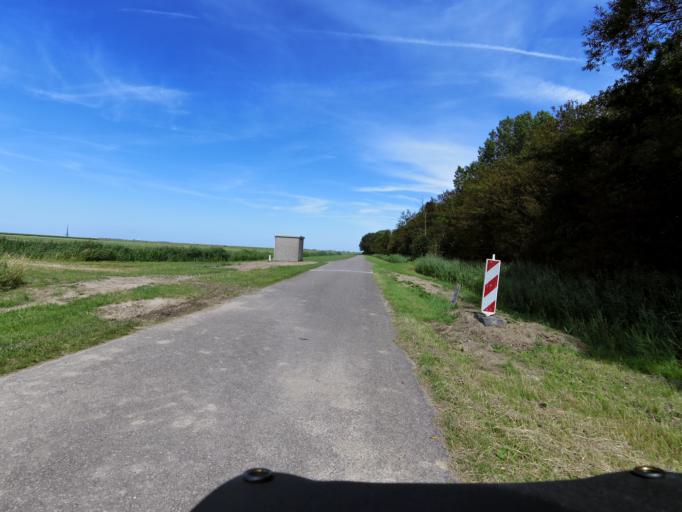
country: NL
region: South Holland
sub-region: Gemeente Goeree-Overflakkee
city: Dirksland
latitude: 51.7879
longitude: 4.1155
